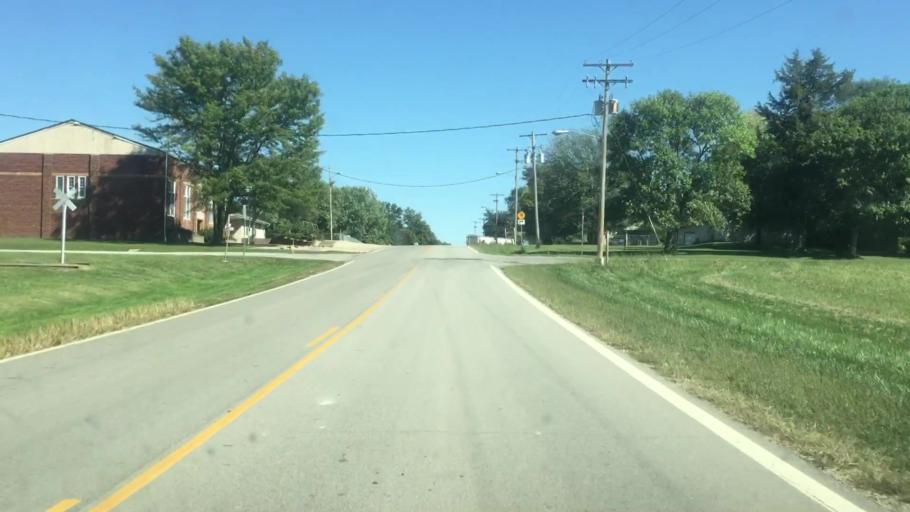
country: US
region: Kansas
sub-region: Brown County
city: Horton
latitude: 39.5930
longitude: -95.6144
